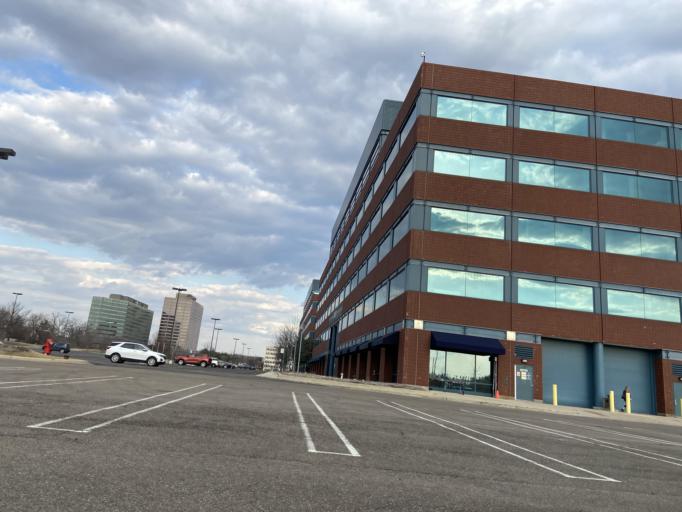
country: US
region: Michigan
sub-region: Oakland County
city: Southfield
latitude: 42.4821
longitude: -83.2510
